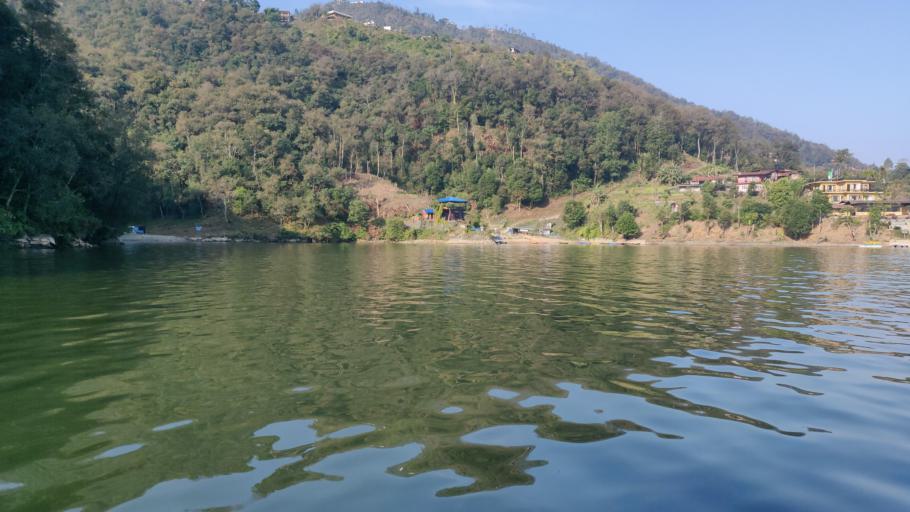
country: NP
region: Western Region
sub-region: Gandaki Zone
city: Pokhara
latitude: 28.2071
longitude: 83.9500
